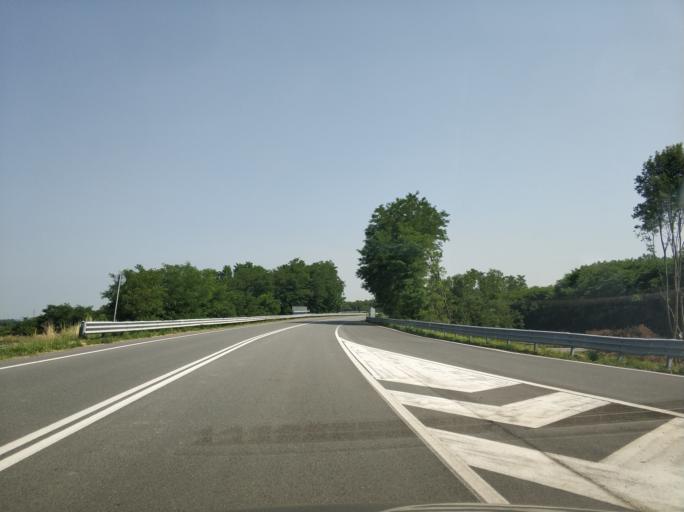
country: IT
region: Piedmont
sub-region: Provincia di Torino
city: Oglianico
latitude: 45.3554
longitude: 7.6977
